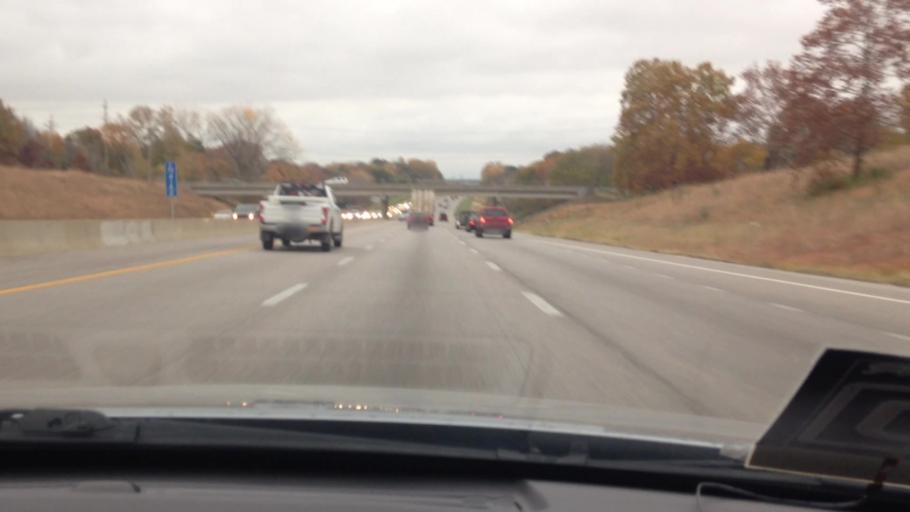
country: US
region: Kansas
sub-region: Johnson County
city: Shawnee
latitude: 39.1058
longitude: -94.7310
